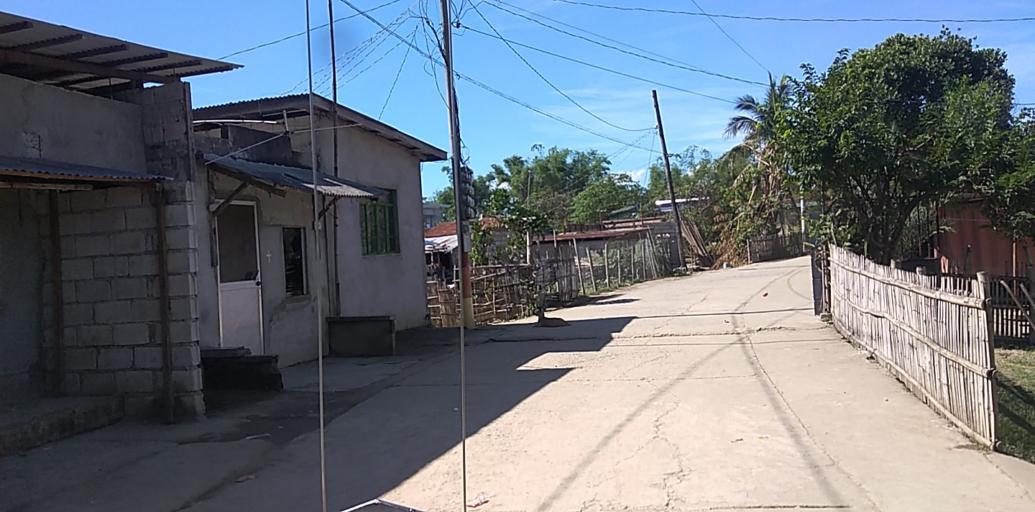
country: PH
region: Central Luzon
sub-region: Province of Pampanga
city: San Nicolas
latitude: 15.0643
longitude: 120.8139
